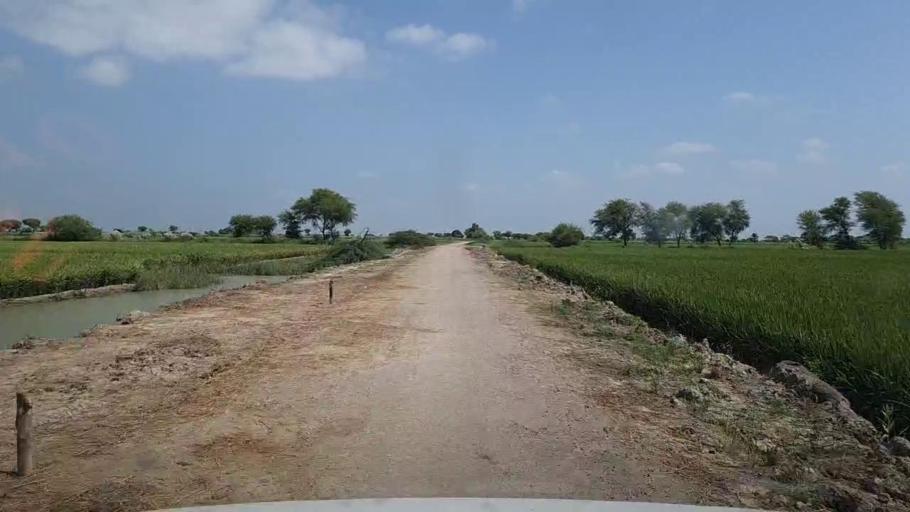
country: PK
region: Sindh
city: Kario
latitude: 24.6843
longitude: 68.5990
